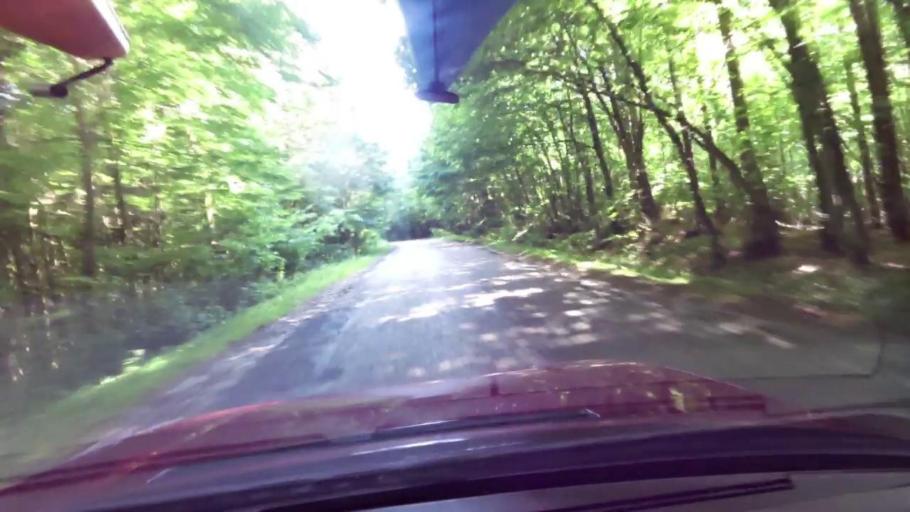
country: PL
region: Pomeranian Voivodeship
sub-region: Powiat slupski
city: Kepice
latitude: 54.1609
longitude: 16.9073
